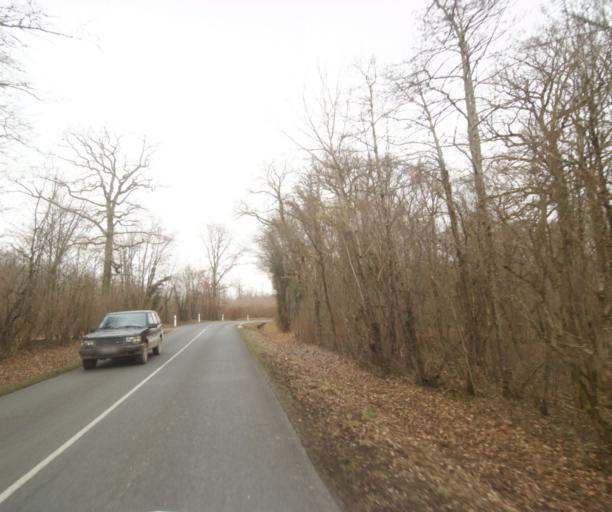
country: FR
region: Champagne-Ardenne
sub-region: Departement de la Marne
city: Pargny-sur-Saulx
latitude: 48.7285
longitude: 4.8673
